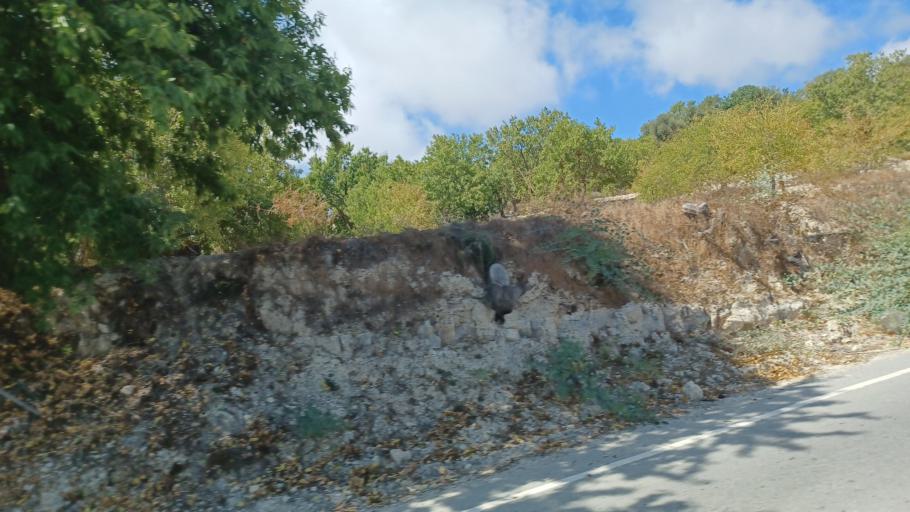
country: CY
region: Pafos
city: Mesogi
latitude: 34.8431
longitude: 32.4647
